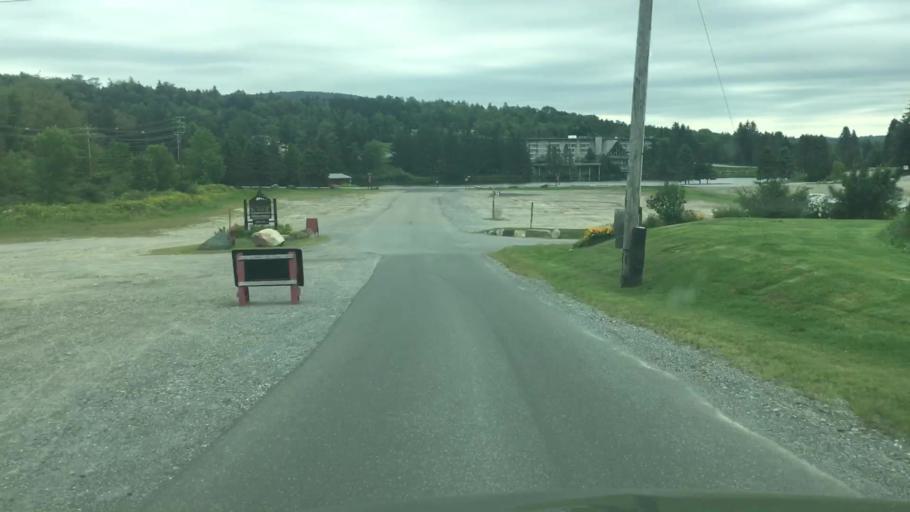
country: US
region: Vermont
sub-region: Windham County
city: Dover
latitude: 42.9673
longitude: -72.8920
